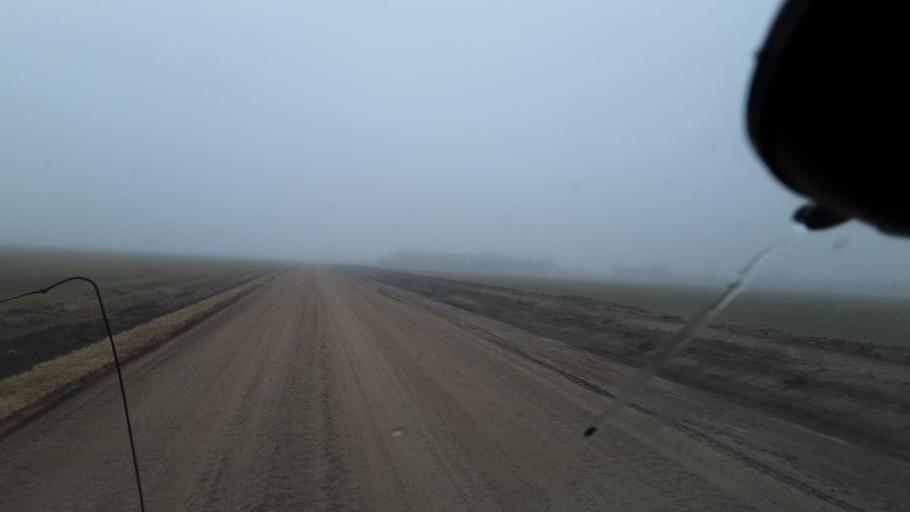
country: US
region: Kansas
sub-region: Reno County
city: South Hutchinson
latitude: 37.9842
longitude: -97.9843
